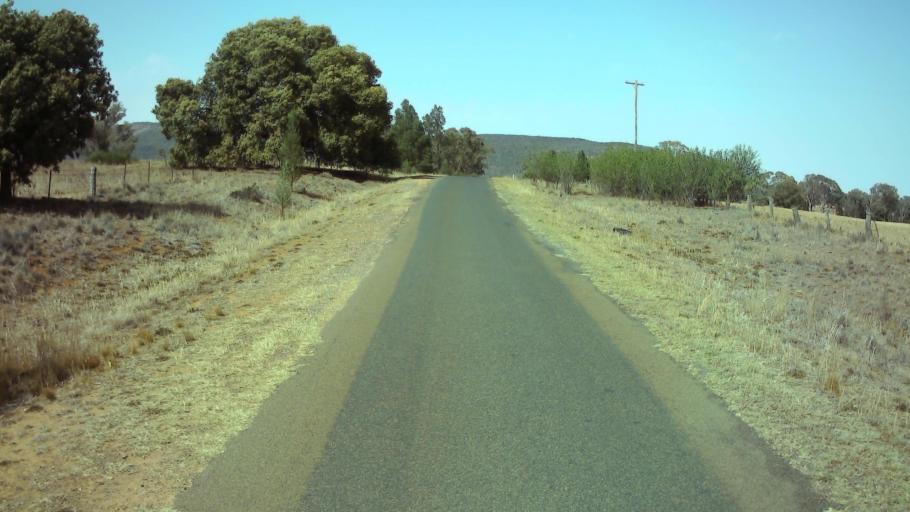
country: AU
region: New South Wales
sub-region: Weddin
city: Grenfell
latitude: -33.8645
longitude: 148.0102
